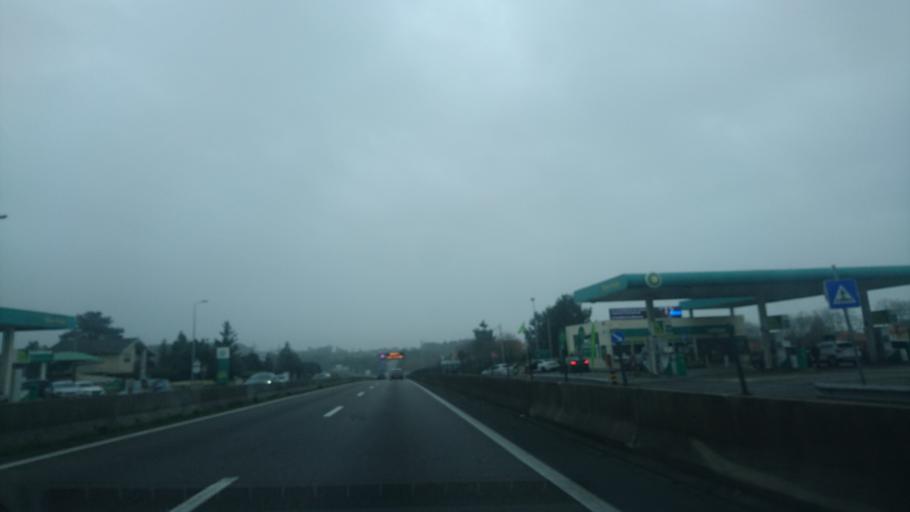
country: PT
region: Porto
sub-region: Vila Nova de Gaia
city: Vilar do Paraiso
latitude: 41.0941
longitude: -8.6293
